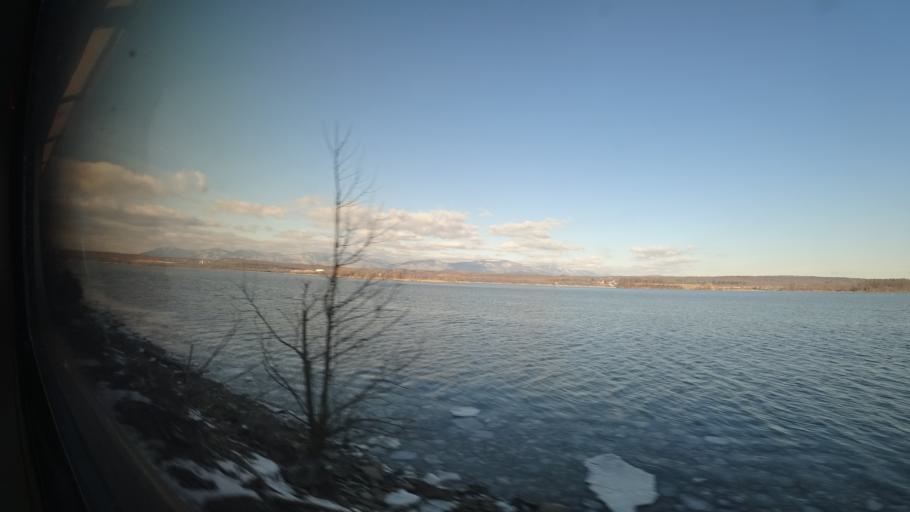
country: US
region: New York
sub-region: Greene County
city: Catskill
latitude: 42.1674
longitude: -73.8764
